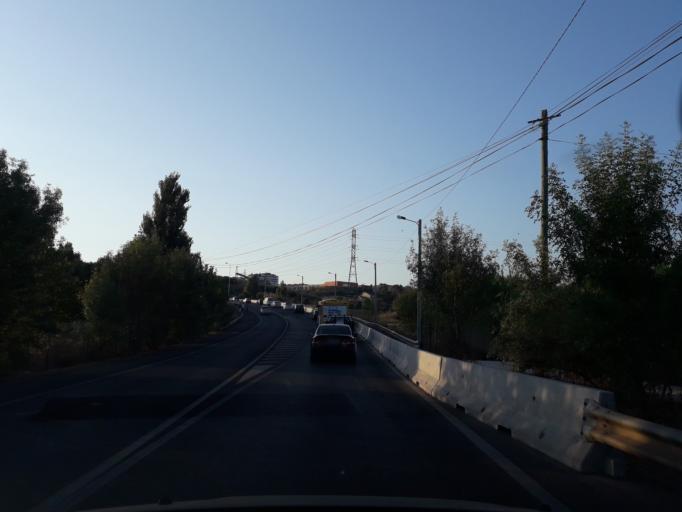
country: PT
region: Lisbon
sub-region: Odivelas
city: Pontinha
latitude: 38.7737
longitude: -9.2044
